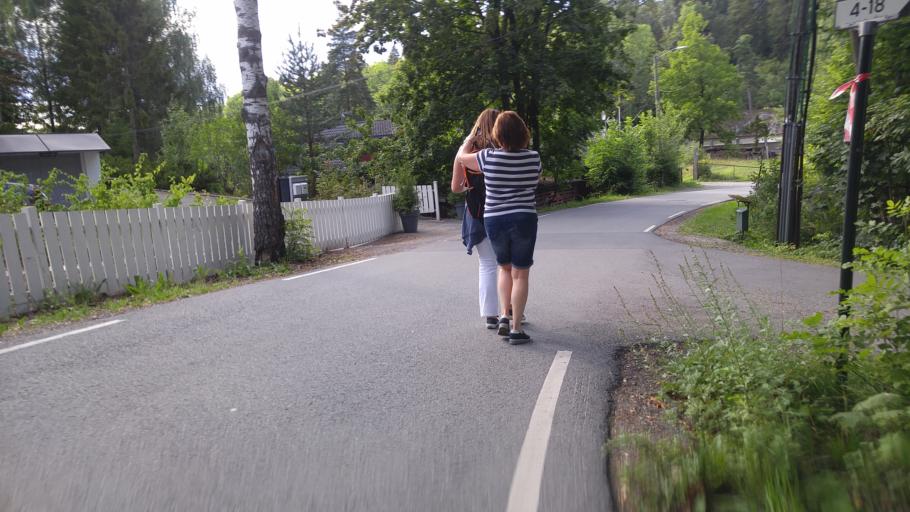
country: NO
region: Akershus
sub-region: Asker
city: Billingstad
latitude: 59.8486
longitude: 10.4917
